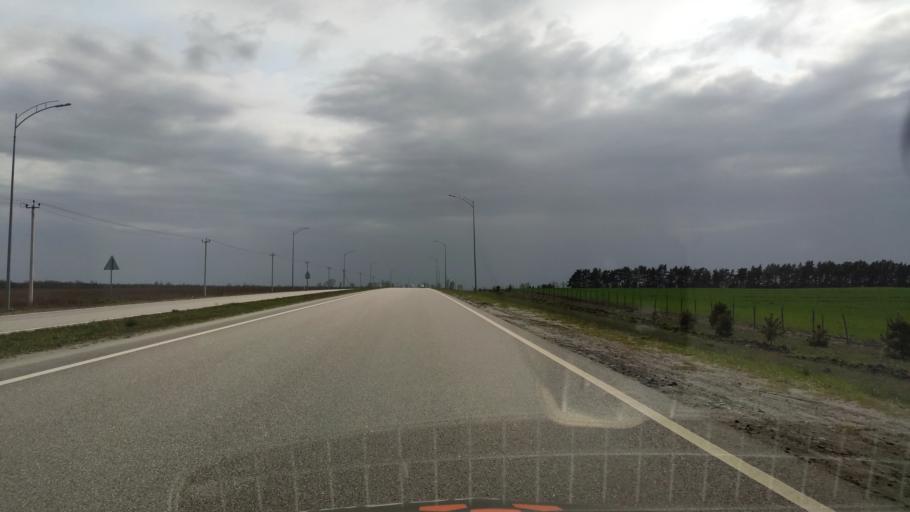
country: RU
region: Belgorod
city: Staryy Oskol
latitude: 51.3985
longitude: 37.8737
